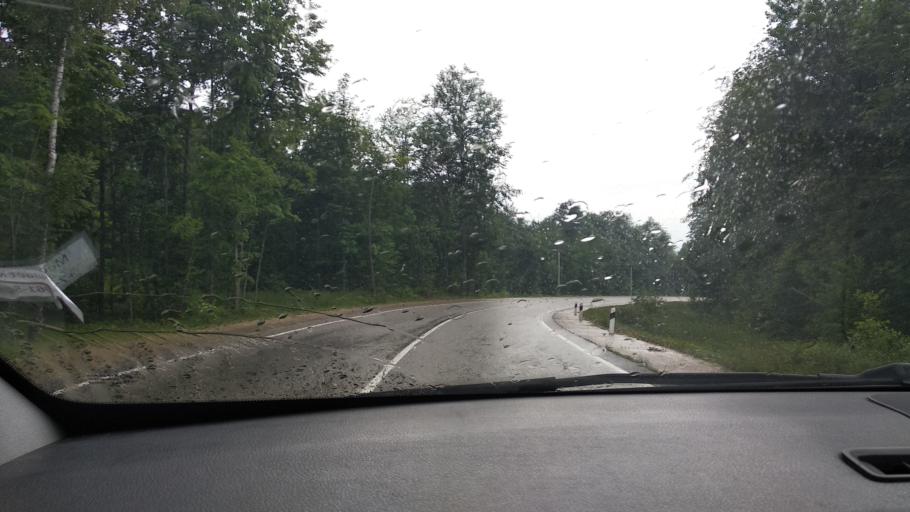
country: RU
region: Adygeya
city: Kamennomostskiy
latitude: 44.2334
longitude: 39.9830
